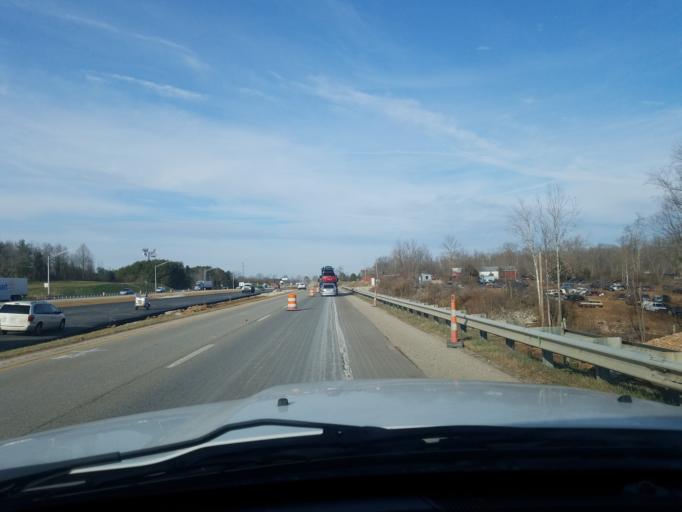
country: US
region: Indiana
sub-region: Monroe County
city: Bloomington
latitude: 39.2690
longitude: -86.5227
